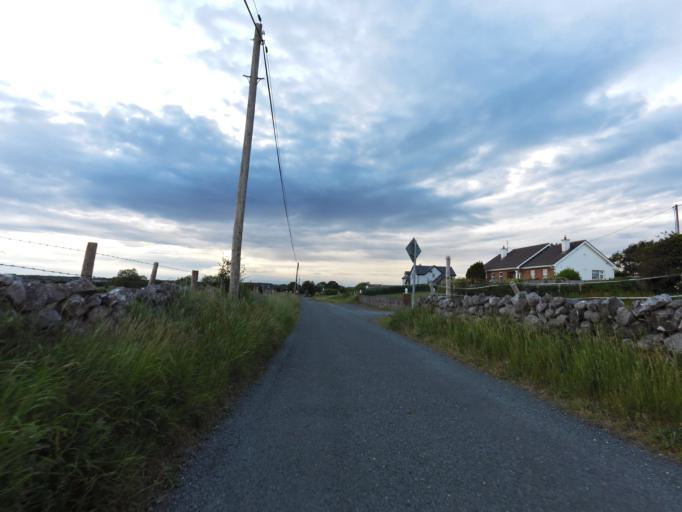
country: IE
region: Connaught
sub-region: County Galway
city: Athenry
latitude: 53.2918
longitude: -8.7192
